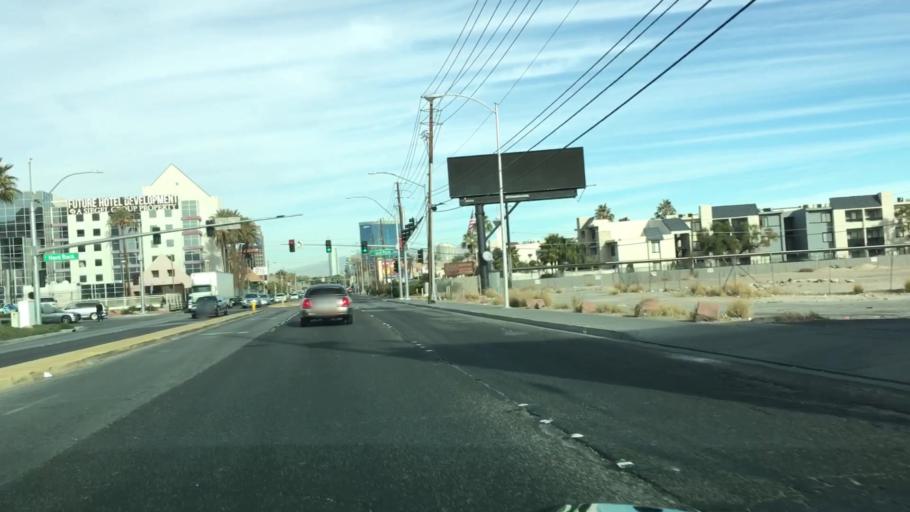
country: US
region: Nevada
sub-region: Clark County
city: Paradise
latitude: 36.1105
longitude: -115.1528
